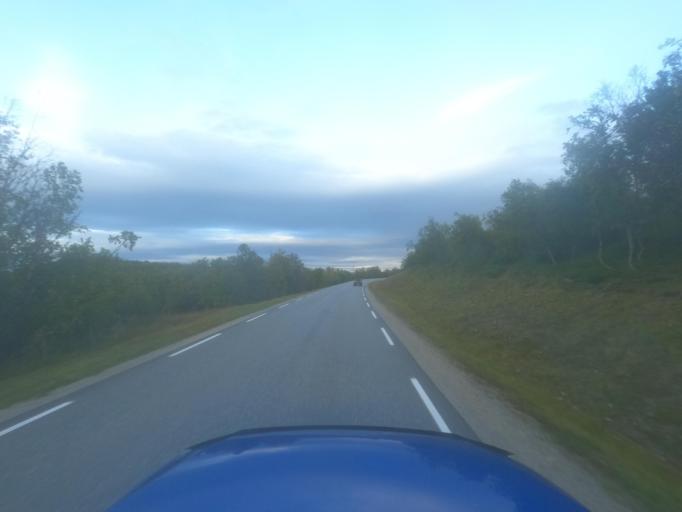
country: NO
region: Finnmark Fylke
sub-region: Porsanger
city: Lakselv
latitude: 70.3485
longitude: 25.0634
